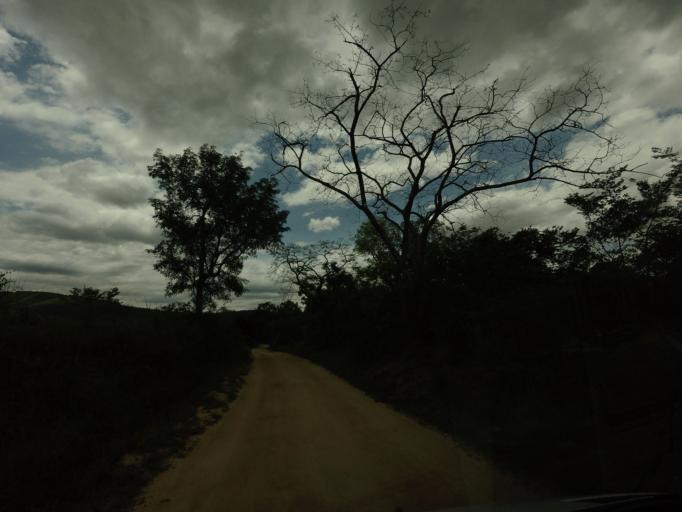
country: ZA
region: Mpumalanga
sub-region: Ehlanzeni District
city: Graksop
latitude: -25.0441
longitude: 31.0794
